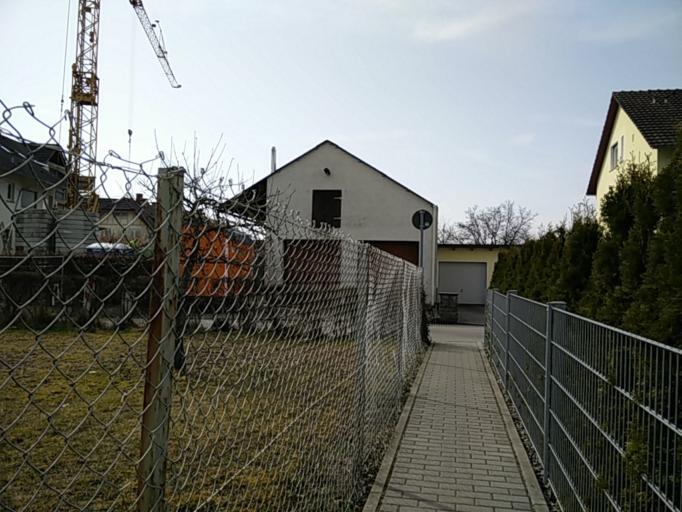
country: DE
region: Baden-Wuerttemberg
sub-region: Freiburg Region
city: Radolfzell am Bodensee
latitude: 47.7417
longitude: 9.0032
